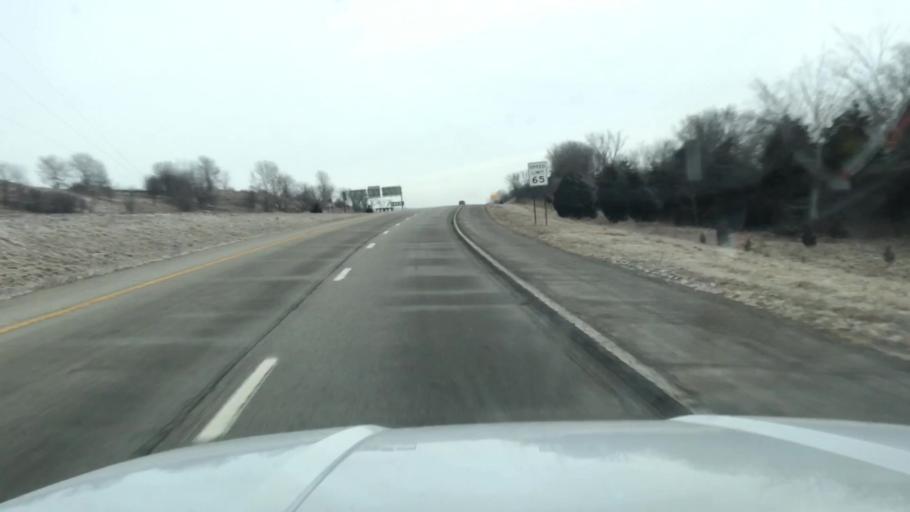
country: US
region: Missouri
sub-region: Andrew County
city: Savannah
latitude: 39.8899
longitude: -94.8570
